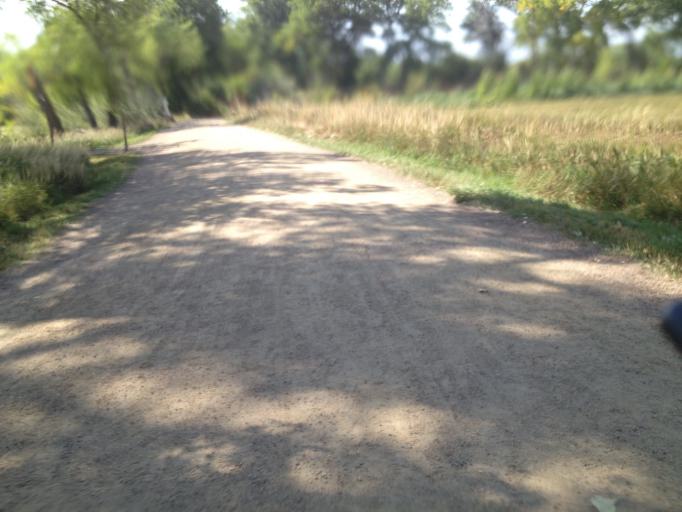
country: US
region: Colorado
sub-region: Boulder County
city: Lafayette
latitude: 39.9972
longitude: -105.1109
